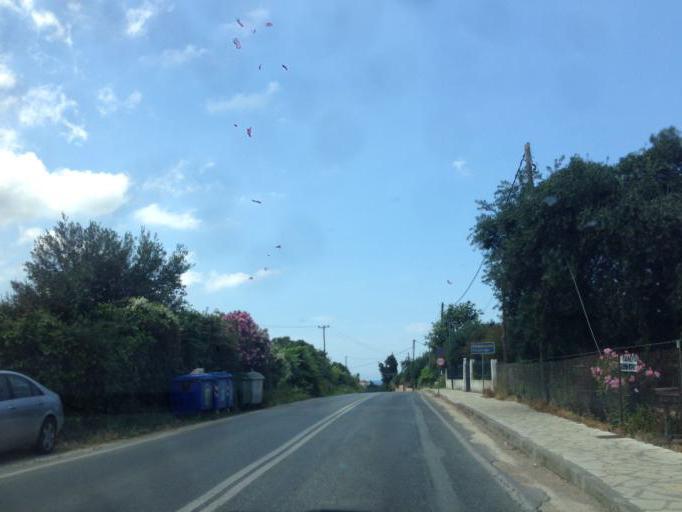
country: GR
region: Ionian Islands
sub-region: Nomos Kerkyras
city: Acharavi
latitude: 39.7830
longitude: 19.9235
